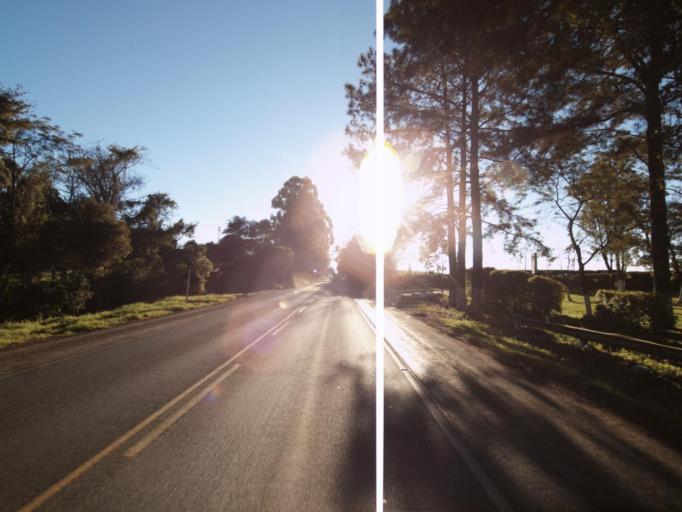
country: BR
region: Santa Catarina
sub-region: Chapeco
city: Chapeco
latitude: -26.8832
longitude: -52.9394
